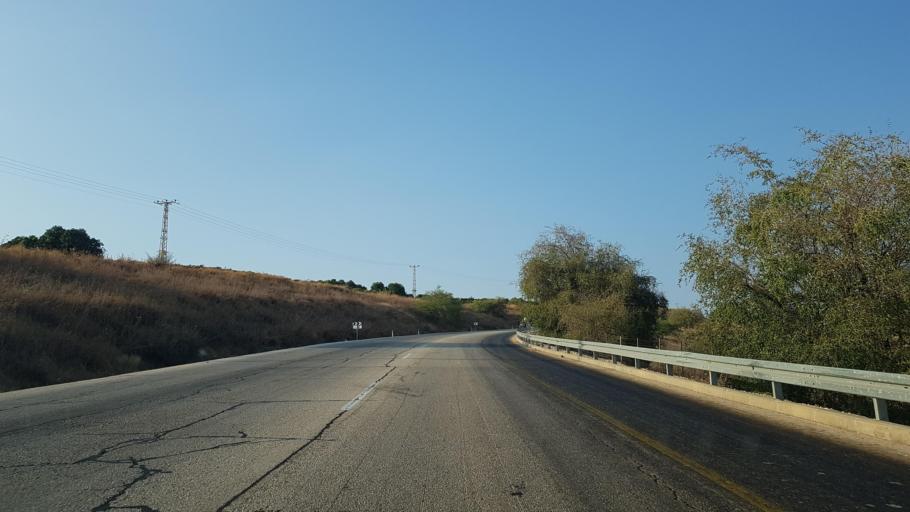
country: SY
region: Quneitra
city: Al Butayhah
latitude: 32.8980
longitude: 35.5969
